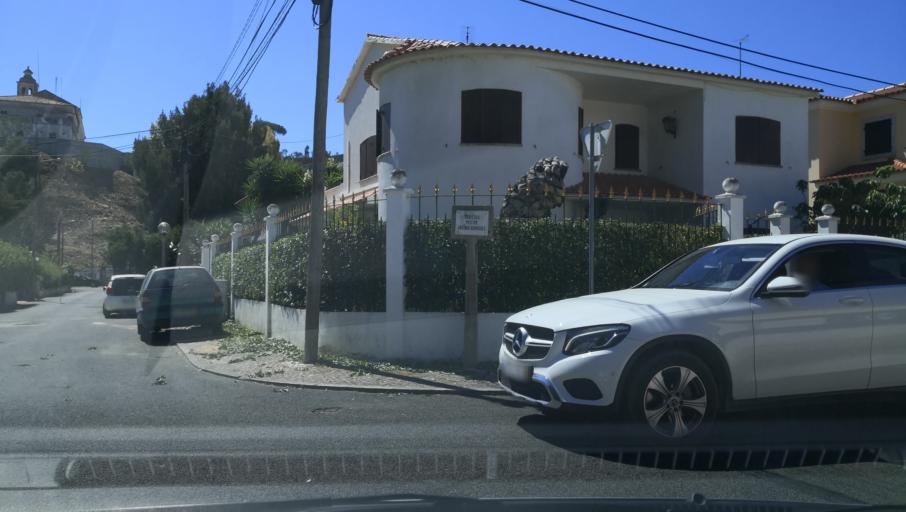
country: PT
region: Setubal
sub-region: Setubal
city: Setubal
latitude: 38.5340
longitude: -8.9027
